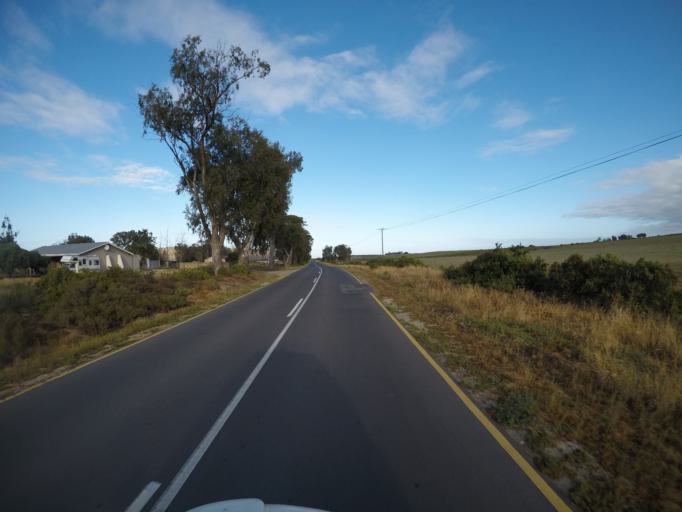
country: ZA
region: Western Cape
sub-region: West Coast District Municipality
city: Clanwilliam
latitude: -32.3115
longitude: 18.3815
